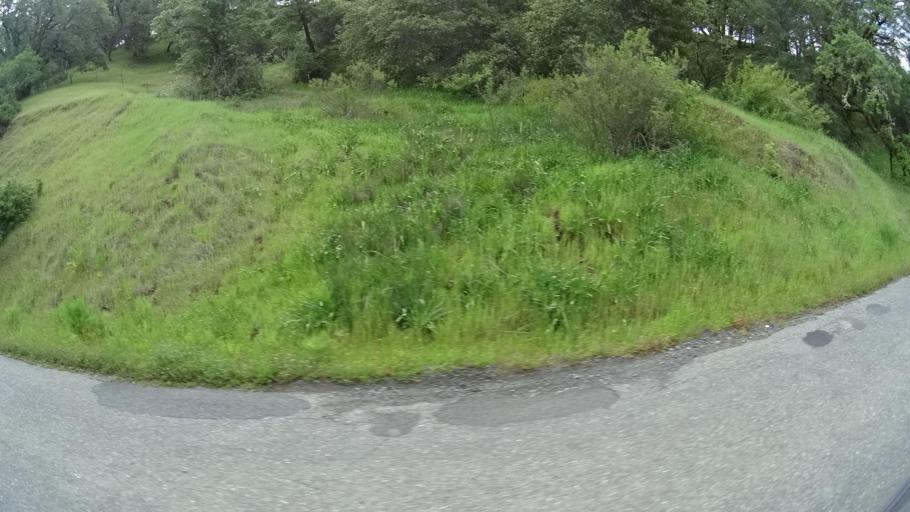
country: US
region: California
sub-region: Humboldt County
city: Redway
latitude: 40.1834
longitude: -123.5907
